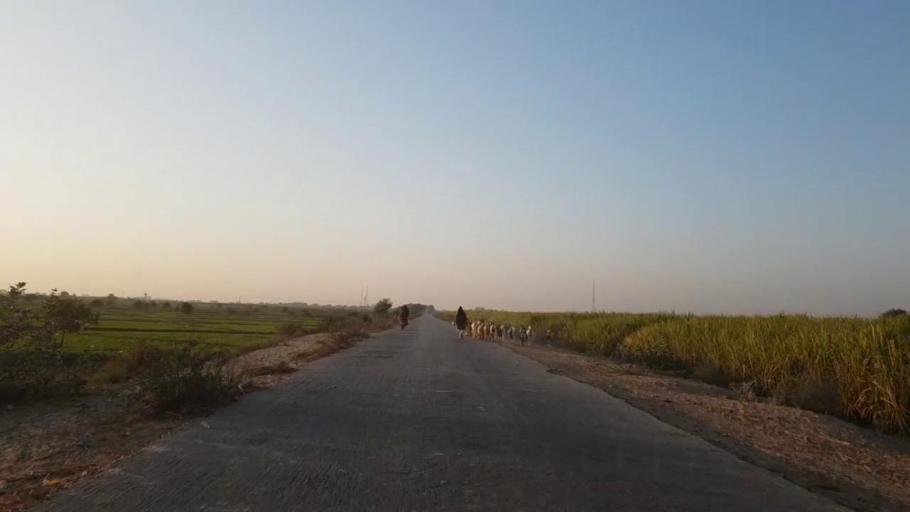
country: PK
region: Sindh
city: Chambar
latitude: 25.2527
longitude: 68.6732
